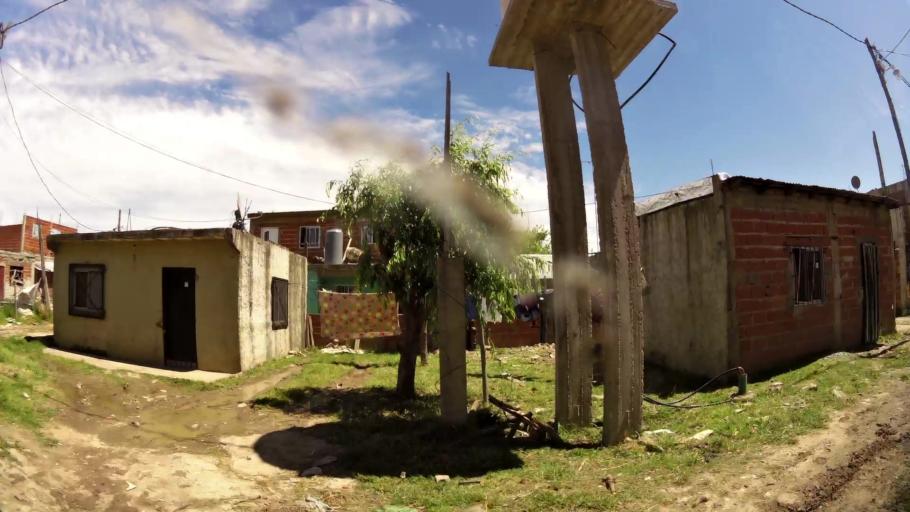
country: AR
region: Buenos Aires
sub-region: Partido de Quilmes
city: Quilmes
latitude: -34.7354
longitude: -58.3126
